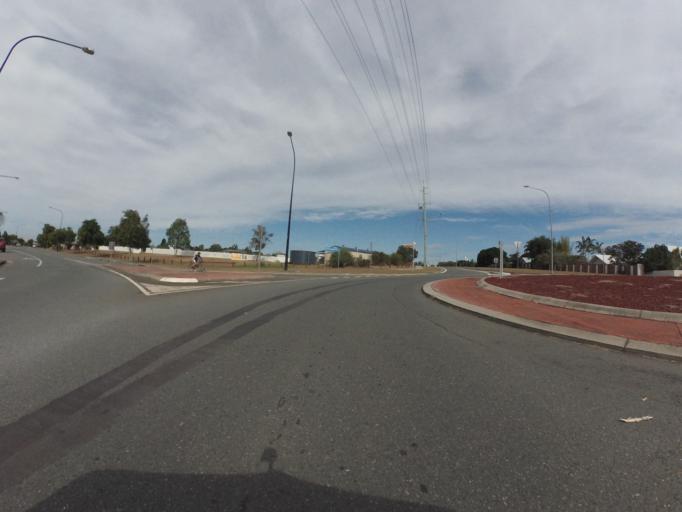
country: AU
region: Queensland
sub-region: Brisbane
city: Moggill
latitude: -27.5714
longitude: 152.8734
